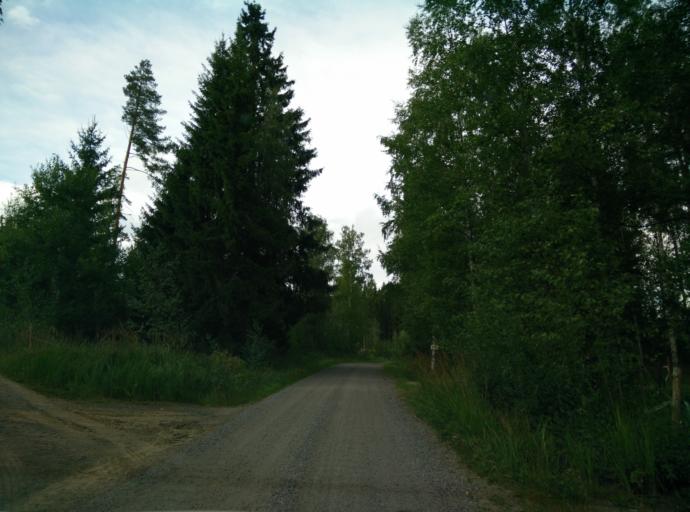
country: FI
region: Haeme
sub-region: Haemeenlinna
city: Kalvola
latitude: 61.1232
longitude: 24.1408
